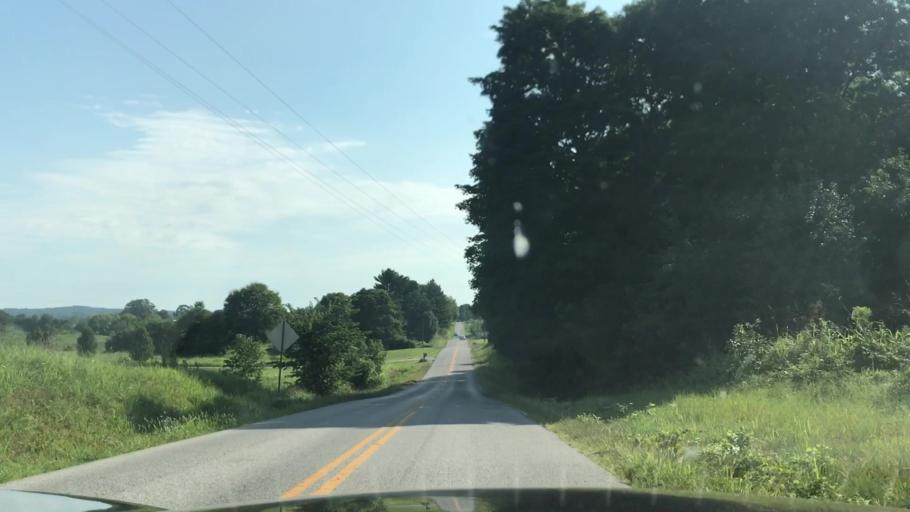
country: US
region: Kentucky
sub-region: Hart County
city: Horse Cave
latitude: 37.1819
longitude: -85.7767
